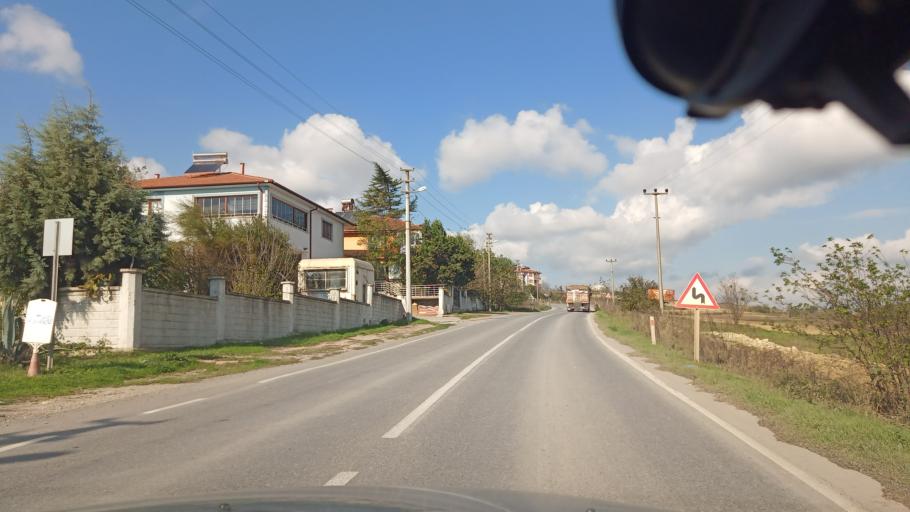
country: TR
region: Sakarya
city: Kaynarca
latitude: 41.0417
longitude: 30.2861
